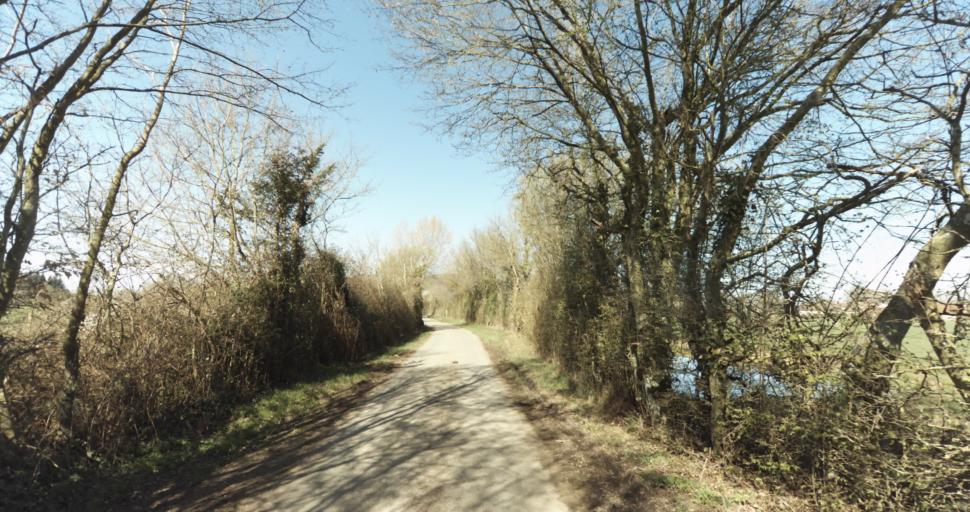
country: FR
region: Lower Normandy
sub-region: Departement du Calvados
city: Livarot
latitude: 49.0211
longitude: 0.1026
